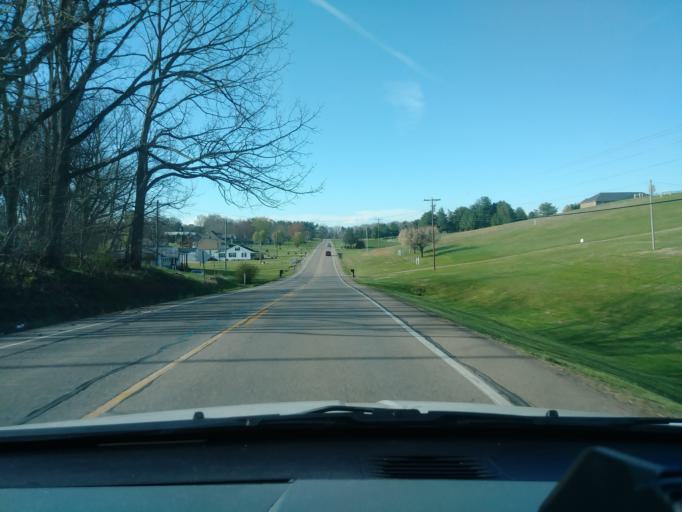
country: US
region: Tennessee
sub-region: Greene County
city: Greeneville
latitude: 36.0748
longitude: -82.8676
